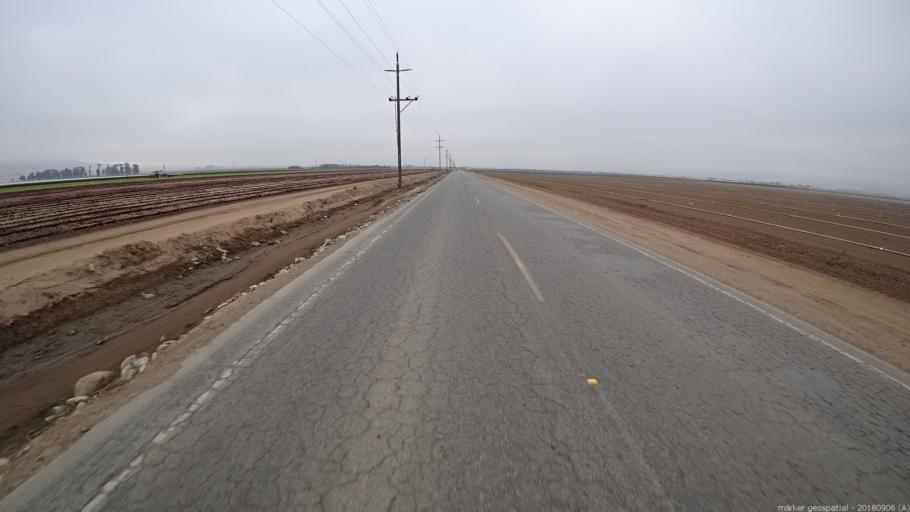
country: US
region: California
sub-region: Monterey County
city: Salinas
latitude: 36.6546
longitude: -121.5850
